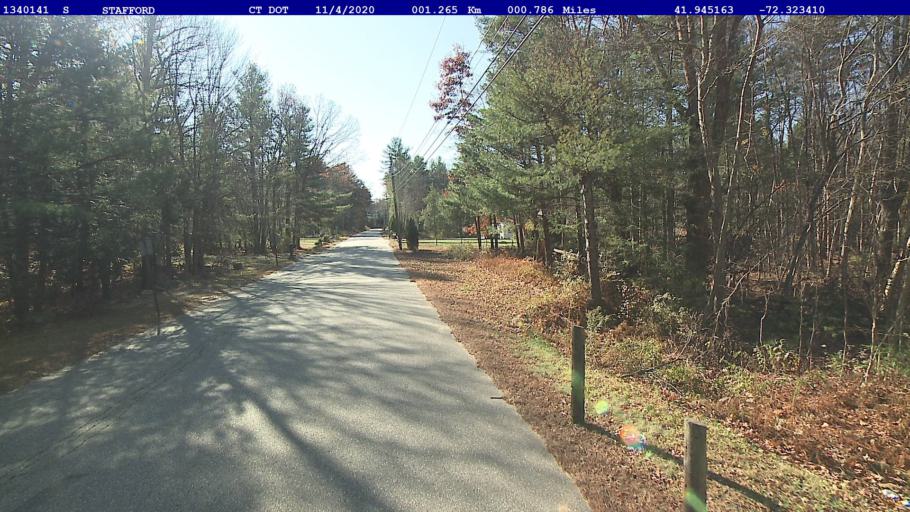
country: US
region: Connecticut
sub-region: Tolland County
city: Stafford Springs
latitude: 41.9452
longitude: -72.3234
